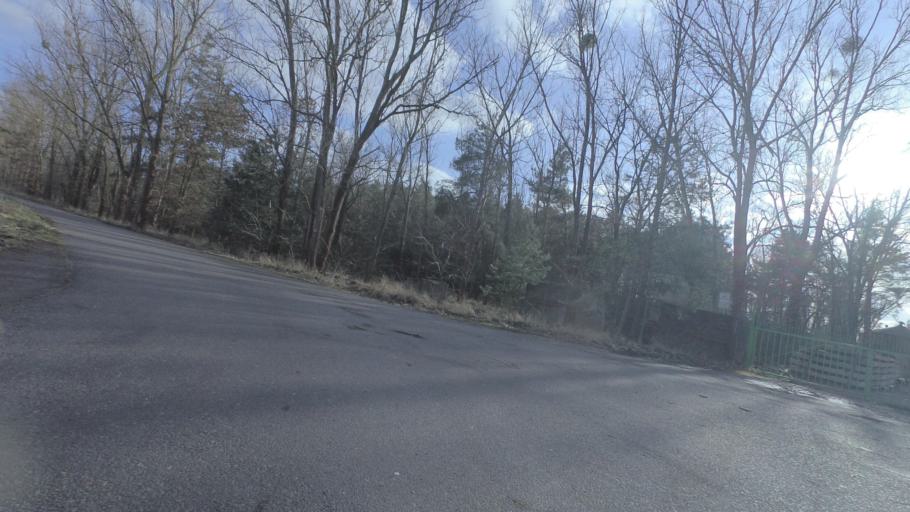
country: DE
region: Brandenburg
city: Trebbin
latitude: 52.2260
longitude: 13.2369
